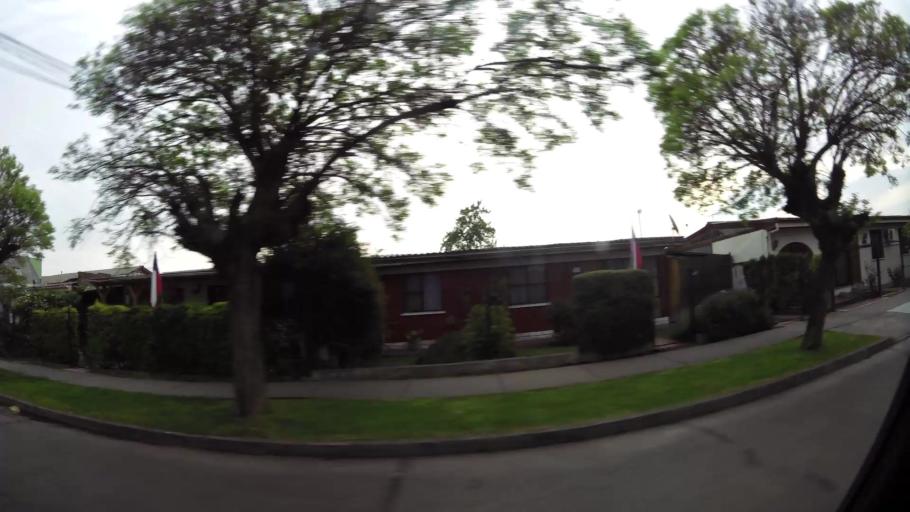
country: CL
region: Santiago Metropolitan
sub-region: Provincia de Santiago
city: Lo Prado
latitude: -33.5143
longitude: -70.7710
